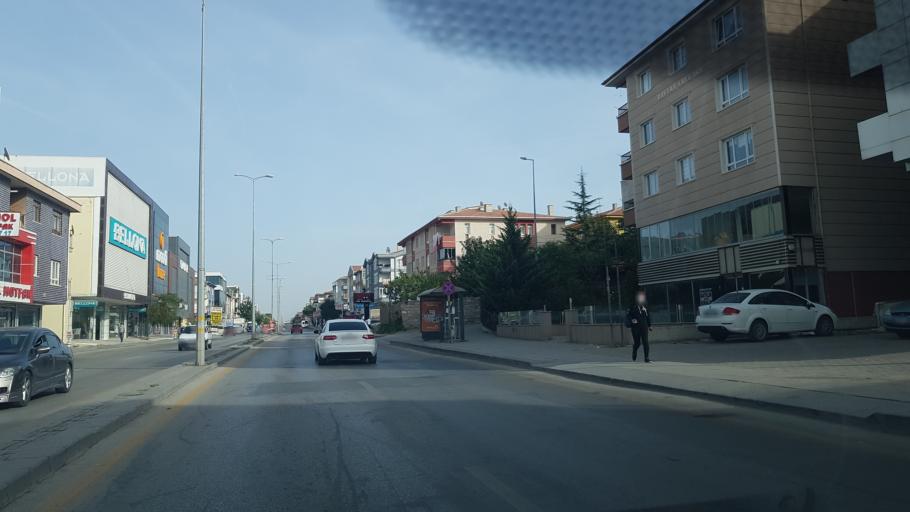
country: TR
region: Ankara
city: Etimesgut
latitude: 39.9507
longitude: 32.6513
